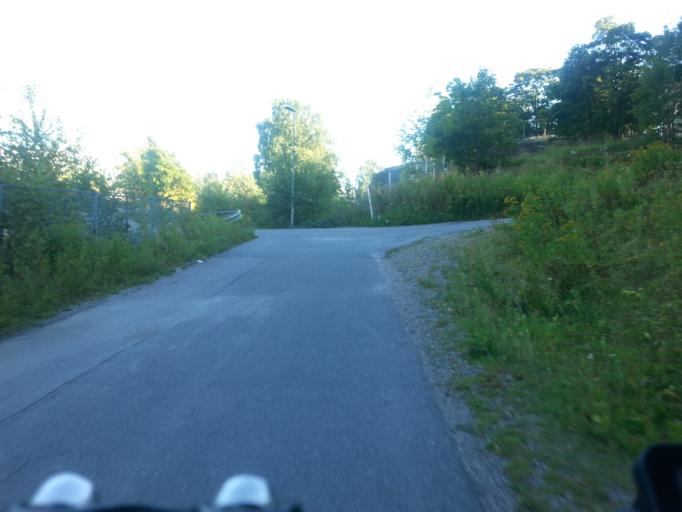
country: FI
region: Uusimaa
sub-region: Helsinki
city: Helsinki
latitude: 60.2038
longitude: 24.9277
